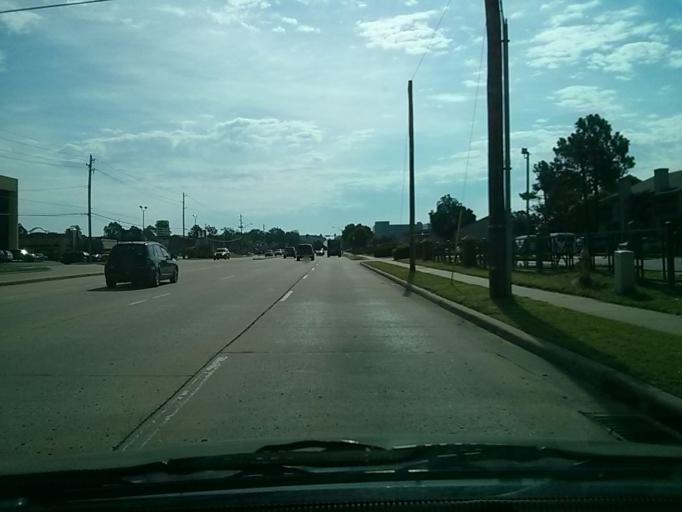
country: US
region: Oklahoma
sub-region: Tulsa County
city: Jenks
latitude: 36.0606
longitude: -95.9715
